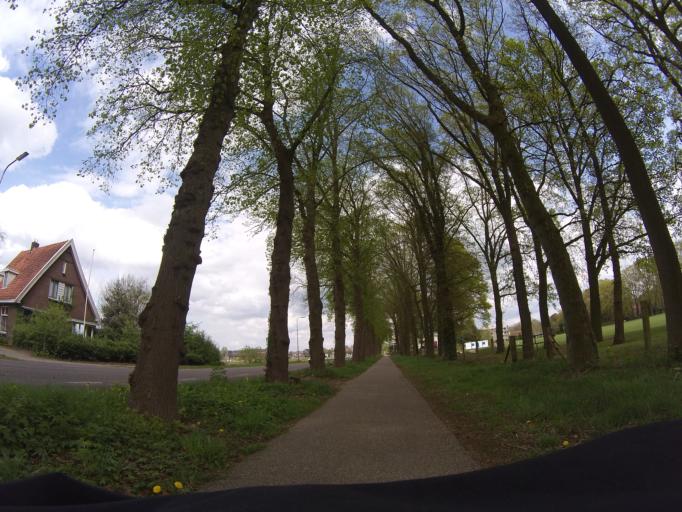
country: NL
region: Overijssel
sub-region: Gemeente Twenterand
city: Den Ham
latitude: 52.5163
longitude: 6.4167
